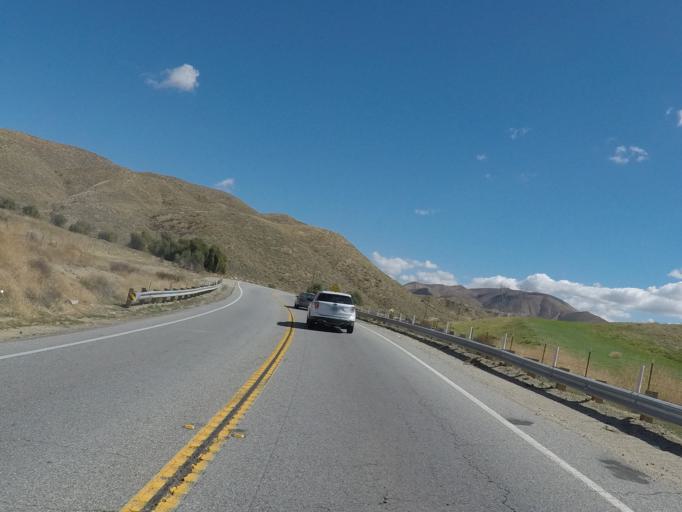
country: US
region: California
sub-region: Riverside County
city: Lakeview
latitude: 33.8664
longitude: -117.0366
